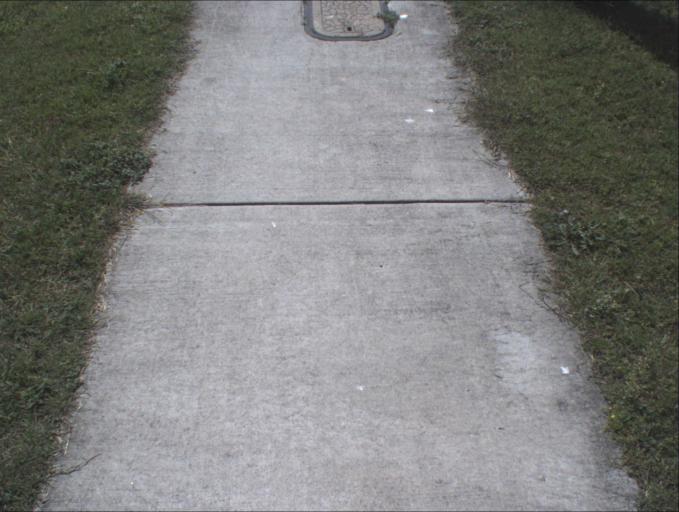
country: AU
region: Queensland
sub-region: Logan
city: Park Ridge South
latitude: -27.7310
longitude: 153.0373
